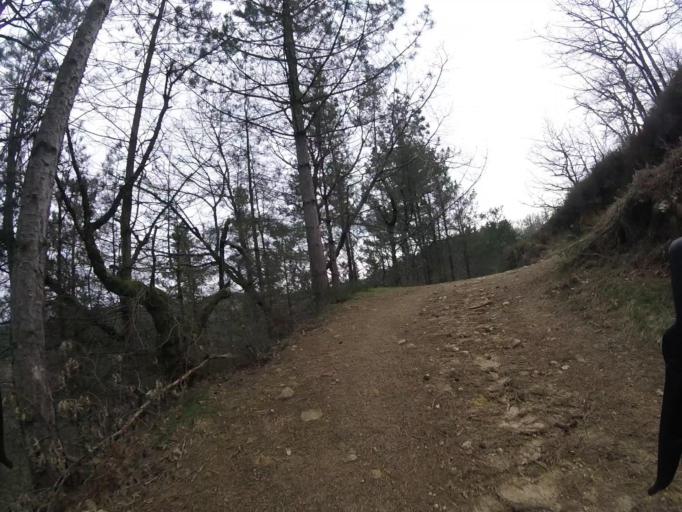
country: ES
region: Navarre
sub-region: Provincia de Navarra
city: Bera
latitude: 43.2870
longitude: -1.7405
